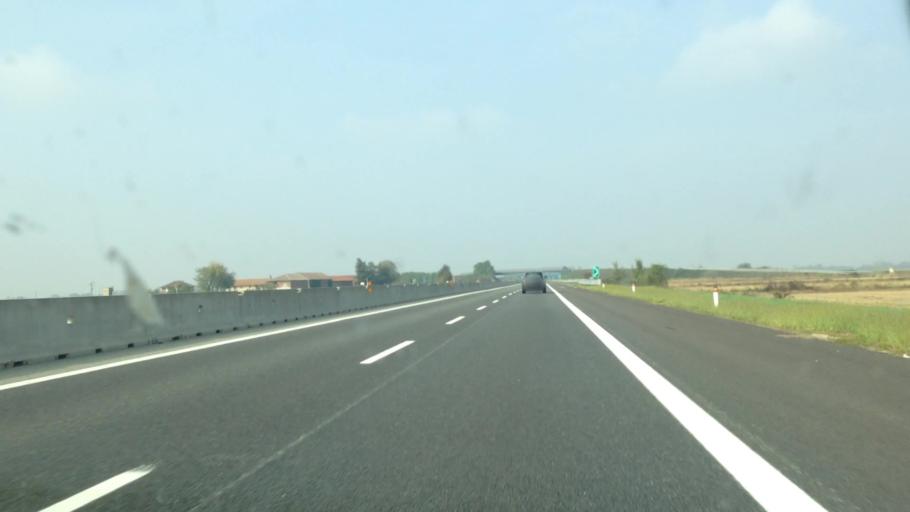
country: IT
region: Piedmont
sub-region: Provincia di Vercelli
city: Salasco
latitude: 45.3222
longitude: 8.2514
